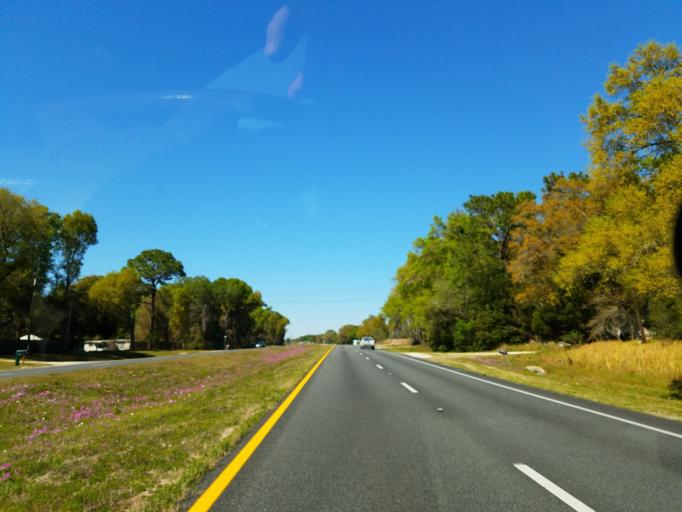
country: US
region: Florida
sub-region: Marion County
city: Belleview
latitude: 29.0319
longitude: -82.0447
